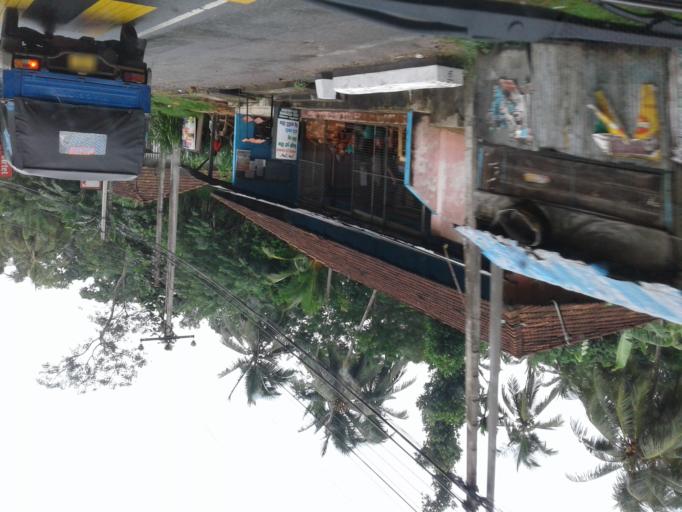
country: LK
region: Central
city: Kadugannawa
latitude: 7.2393
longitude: 80.3221
